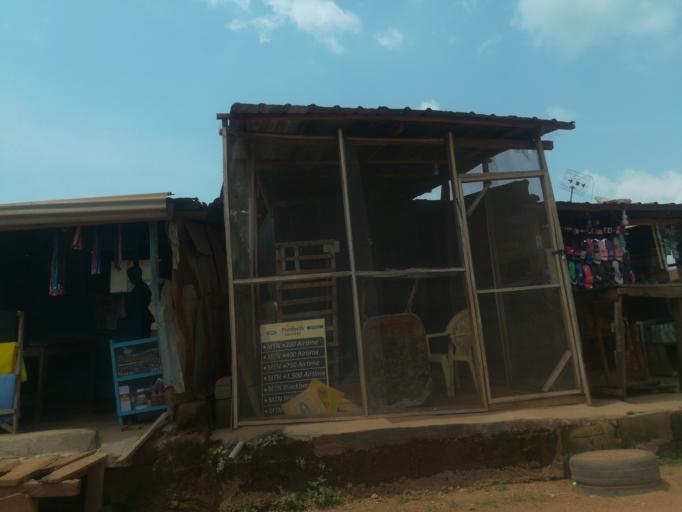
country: NG
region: Oyo
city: Moniya
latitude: 7.4567
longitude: 3.9653
